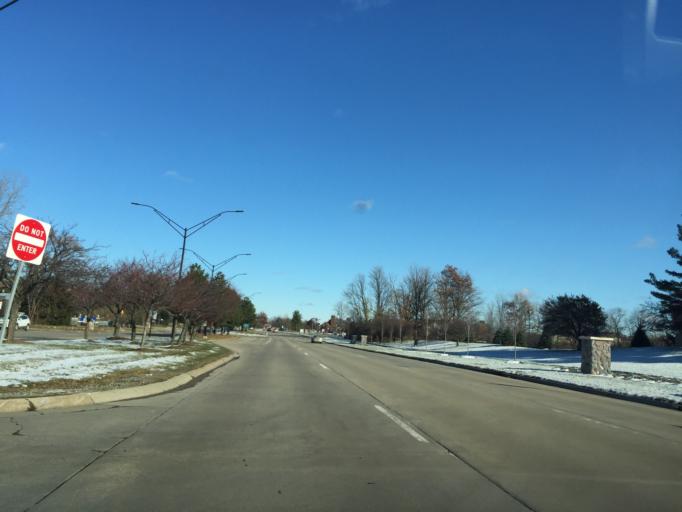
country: US
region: Michigan
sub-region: Oakland County
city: Auburn Hills
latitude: 42.6700
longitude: -83.2322
